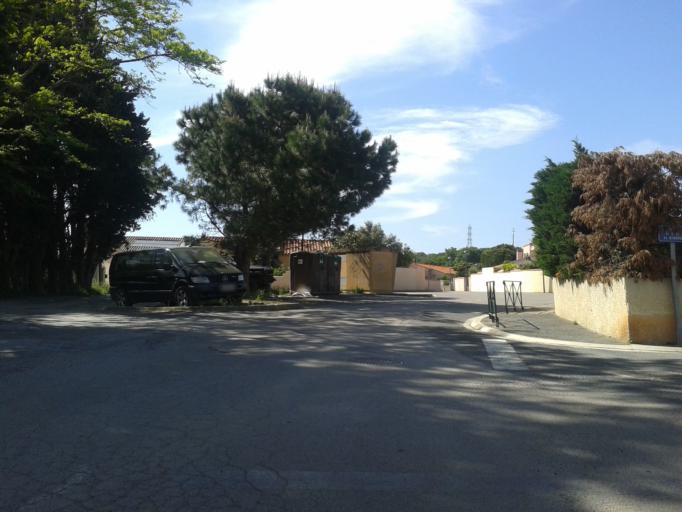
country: FR
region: Languedoc-Roussillon
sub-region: Departement des Pyrenees-Orientales
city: Corneilla-la-Riviere
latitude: 42.6996
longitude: 2.7311
